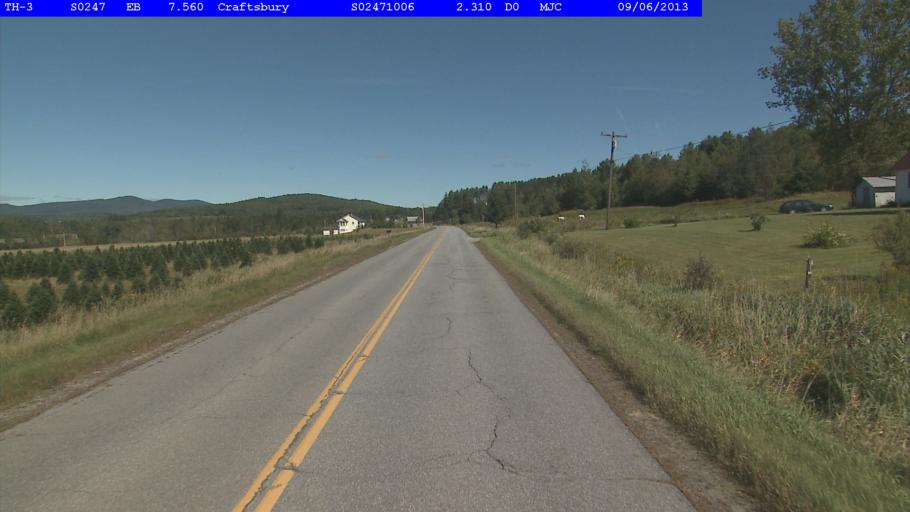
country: US
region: Vermont
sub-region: Caledonia County
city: Hardwick
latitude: 44.6446
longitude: -72.4180
